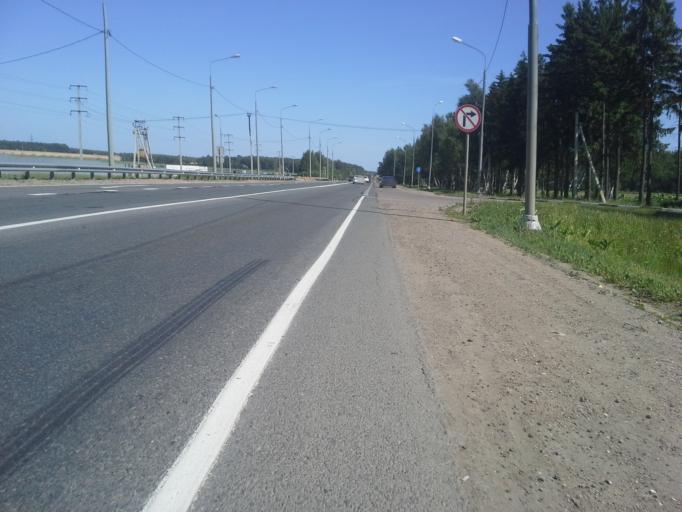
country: RU
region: Moskovskaya
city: Troitsk
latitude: 55.4043
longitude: 37.2132
